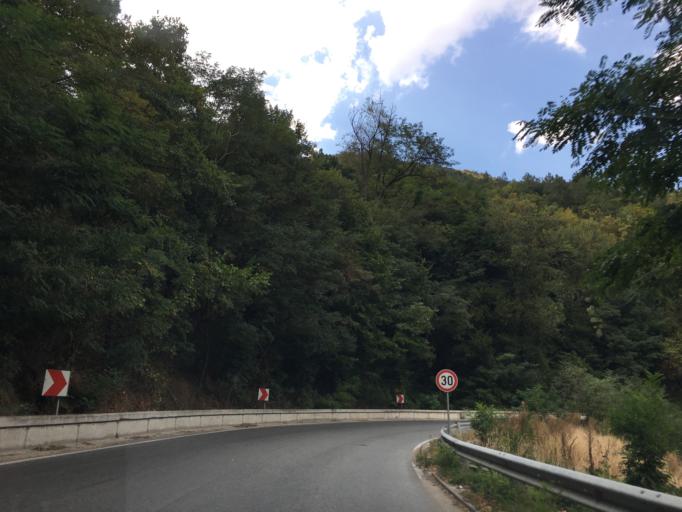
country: BG
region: Pazardzhik
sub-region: Obshtina Septemvri
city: Septemvri
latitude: 42.1311
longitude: 24.1235
